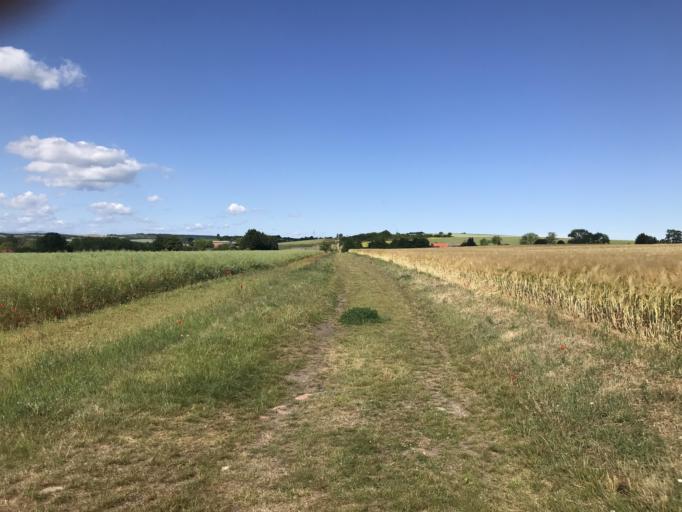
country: DE
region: Saxony-Anhalt
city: Schwanebeck
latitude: 51.9733
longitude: 11.1280
